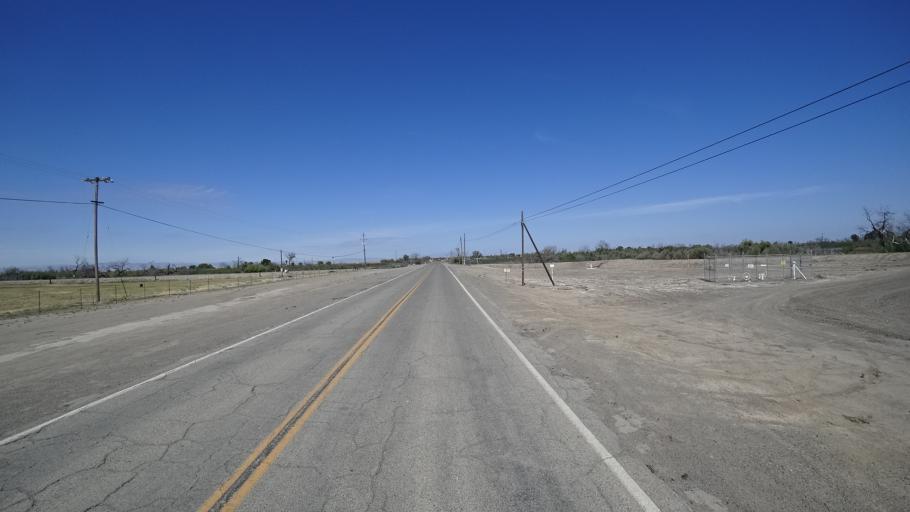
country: US
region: California
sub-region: Kings County
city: Lemoore Station
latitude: 36.2554
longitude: -119.8526
